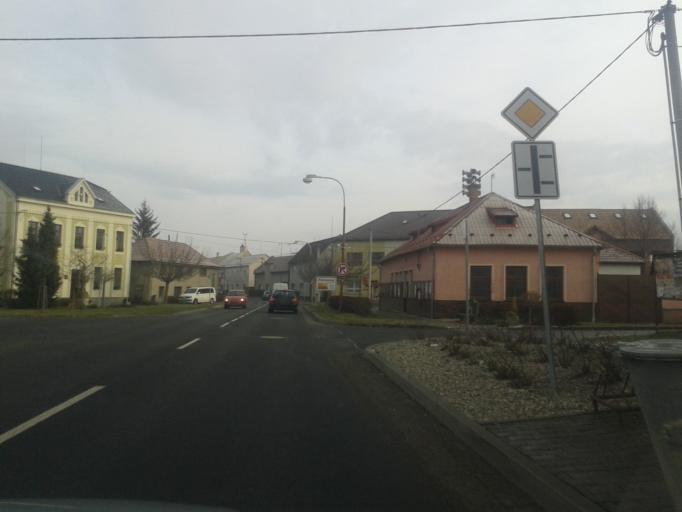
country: CZ
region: Olomoucky
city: Smrzice
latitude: 49.5040
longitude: 17.1013
